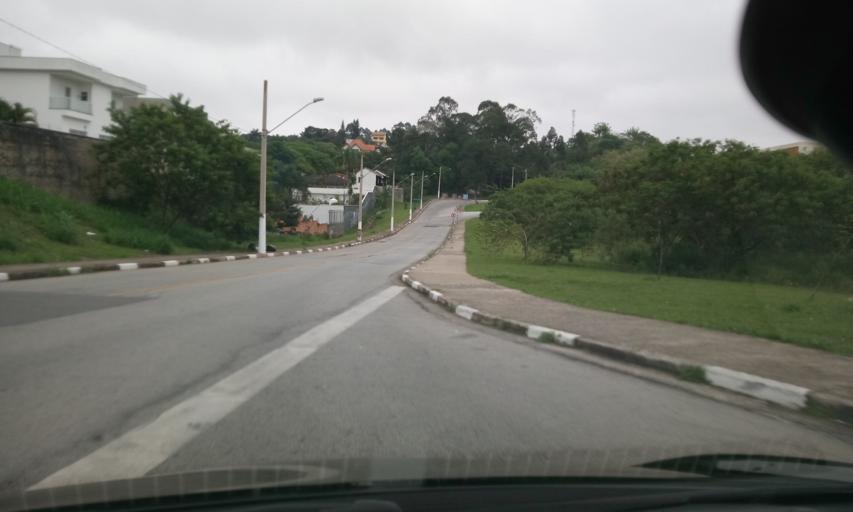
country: BR
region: Sao Paulo
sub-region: Sao Bernardo Do Campo
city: Sao Bernardo do Campo
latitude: -23.6791
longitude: -46.5617
